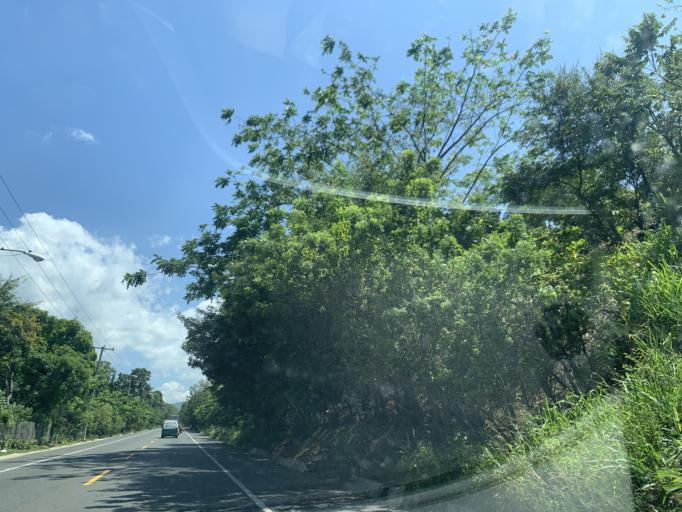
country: DO
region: Puerto Plata
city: Imbert
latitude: 19.7154
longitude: -70.8346
